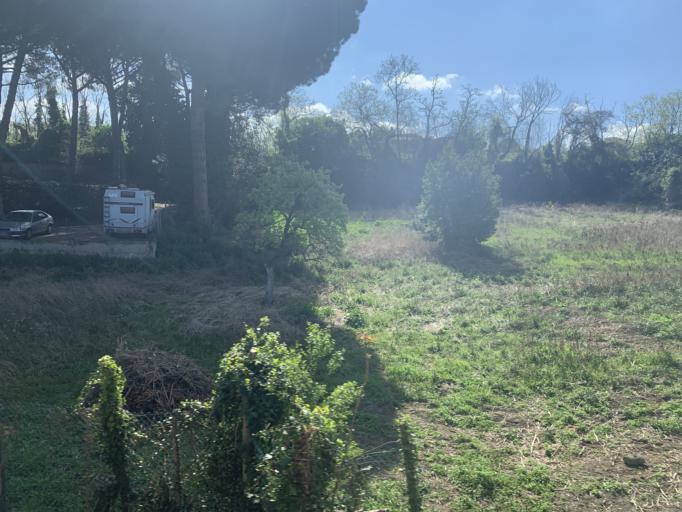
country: IT
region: Latium
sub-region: Citta metropolitana di Roma Capitale
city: Marino
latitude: 41.7741
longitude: 12.6468
